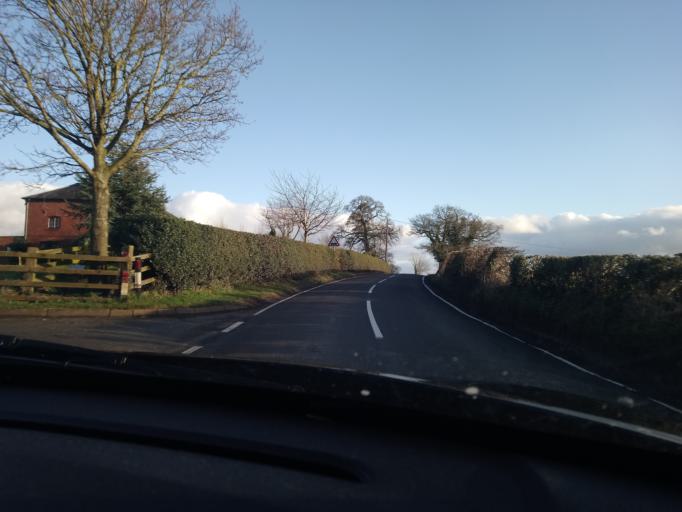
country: GB
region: England
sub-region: Shropshire
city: Wem
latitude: 52.8732
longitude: -2.7794
